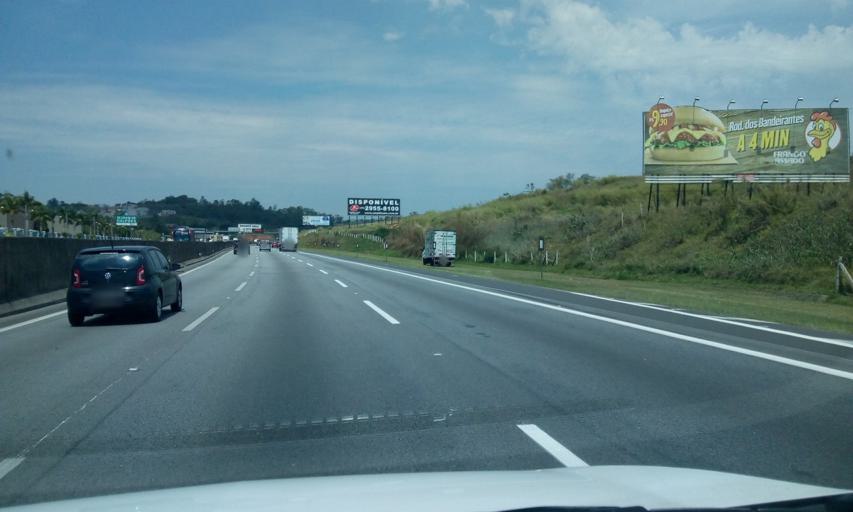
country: BR
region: Sao Paulo
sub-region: Varzea Paulista
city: Varzea Paulista
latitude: -23.2432
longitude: -46.8686
